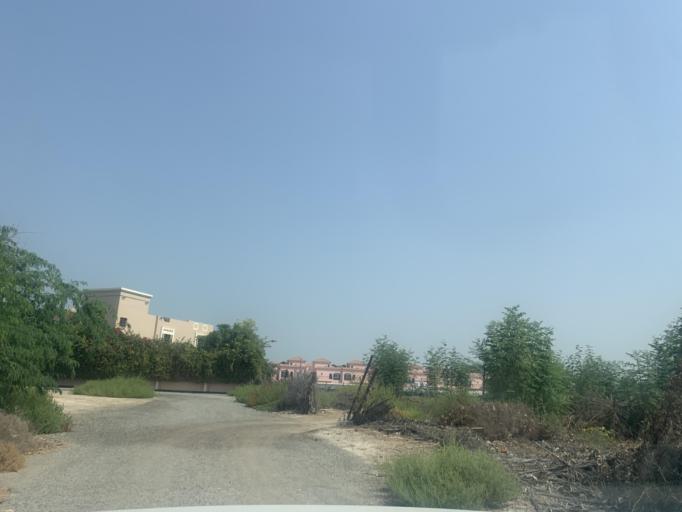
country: BH
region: Central Governorate
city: Madinat Hamad
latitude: 26.1663
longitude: 50.4589
